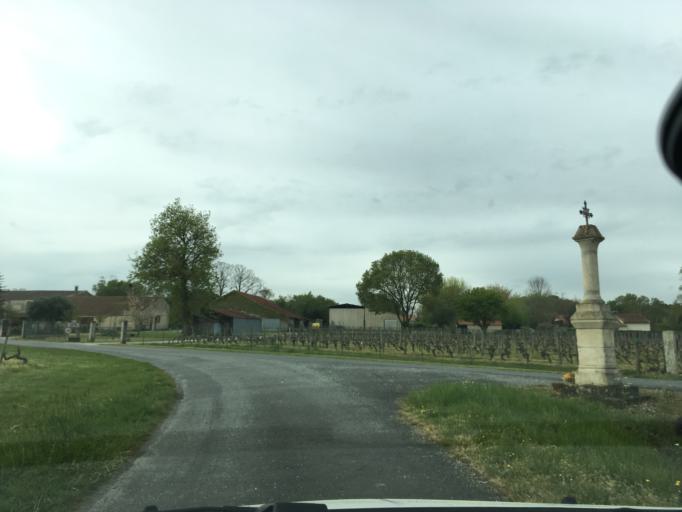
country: FR
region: Aquitaine
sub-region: Departement de la Gironde
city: Lesparre-Medoc
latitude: 45.3147
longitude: -0.8949
